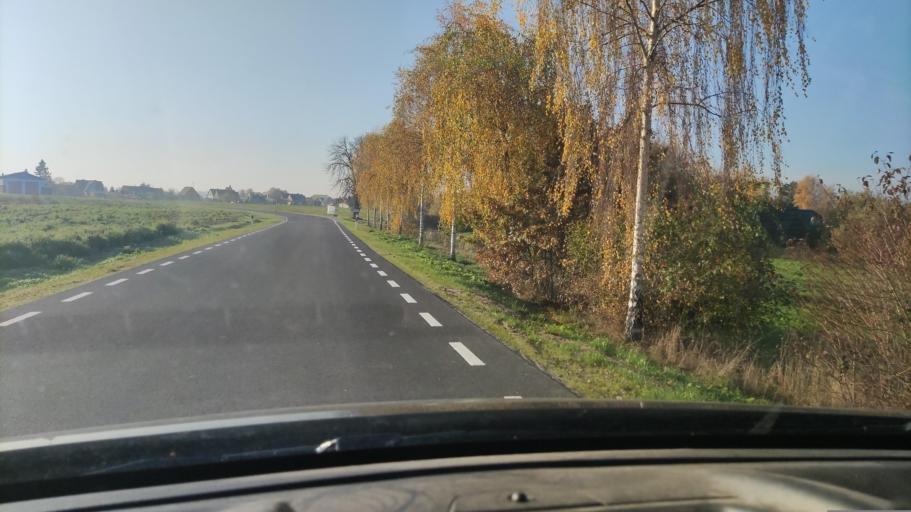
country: DE
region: Mecklenburg-Vorpommern
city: Wesenberg
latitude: 53.2219
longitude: 13.0452
